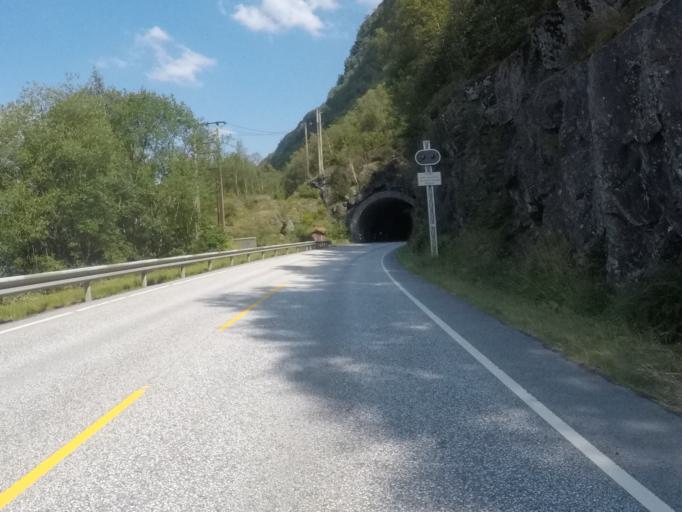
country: NO
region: Sogn og Fjordane
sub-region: Hyllestad
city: Hyllestad
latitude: 61.0321
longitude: 5.4882
